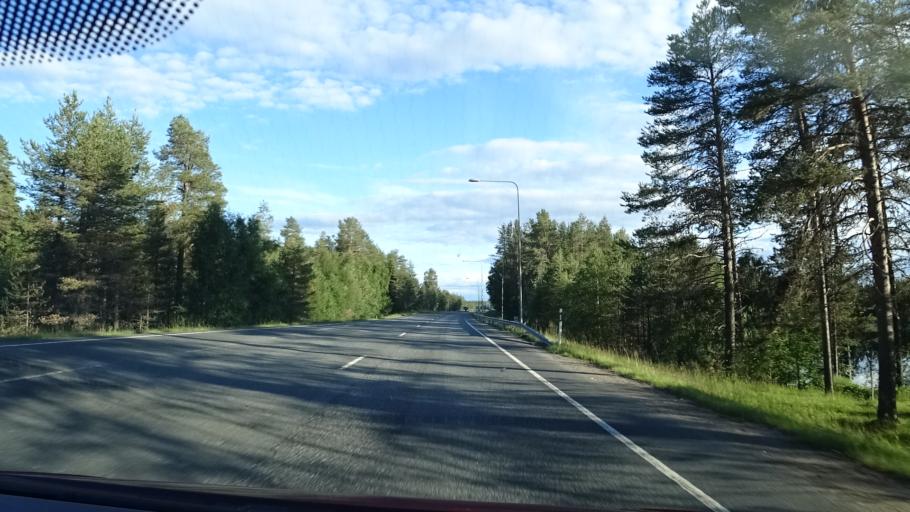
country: FI
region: Northern Ostrobothnia
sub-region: Koillismaa
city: Kuusamo
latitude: 66.0058
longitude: 29.1527
